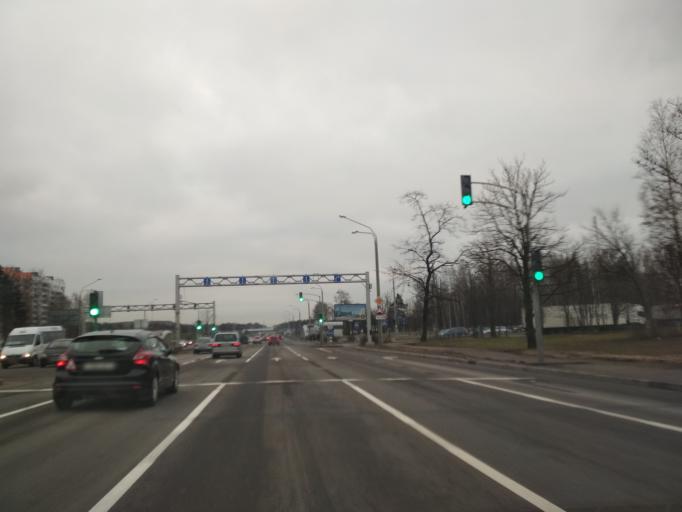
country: BY
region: Minsk
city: Vyaliki Trastsyanets
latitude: 53.8498
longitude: 27.7019
